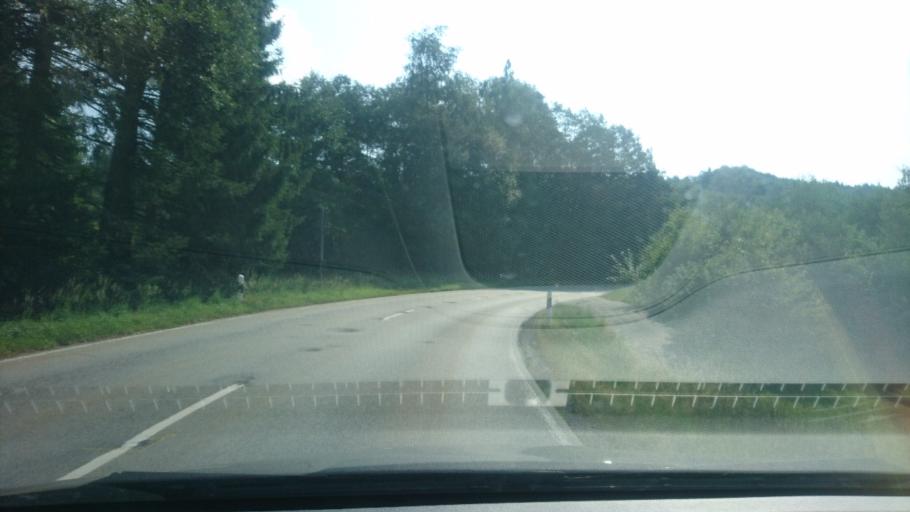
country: DE
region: Bavaria
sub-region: Lower Bavaria
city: Spiegelau
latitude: 48.8987
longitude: 13.3802
